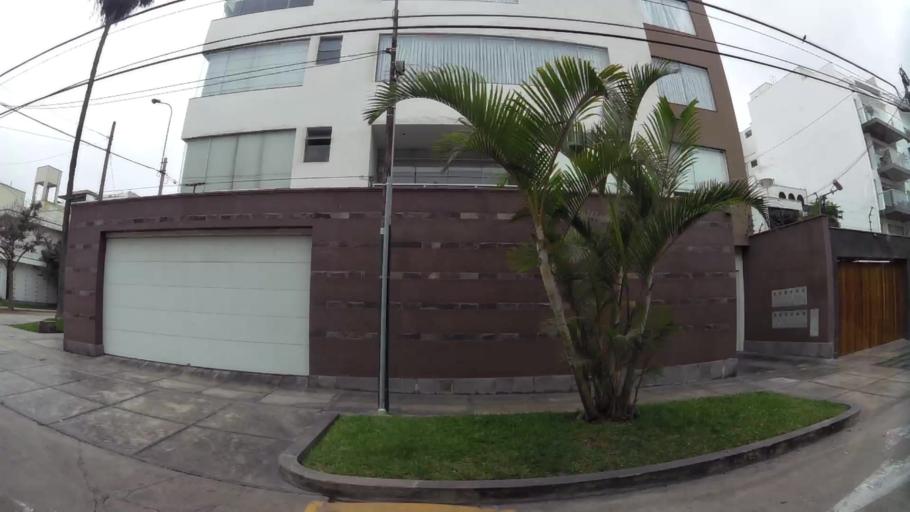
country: PE
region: Lima
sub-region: Lima
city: Surco
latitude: -12.1136
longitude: -76.9853
